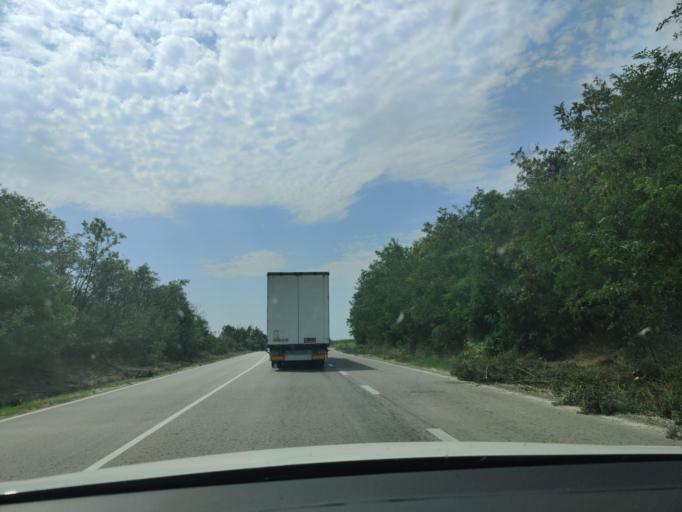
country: BG
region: Vidin
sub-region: Obshtina Vidin
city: Dunavtsi
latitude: 43.8652
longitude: 22.7823
